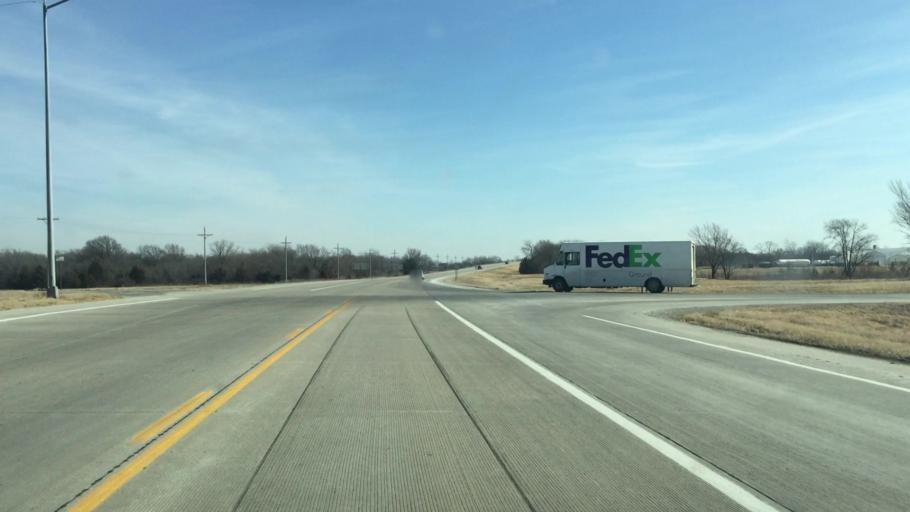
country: US
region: Kansas
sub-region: Labette County
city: Parsons
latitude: 37.3699
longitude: -95.2858
